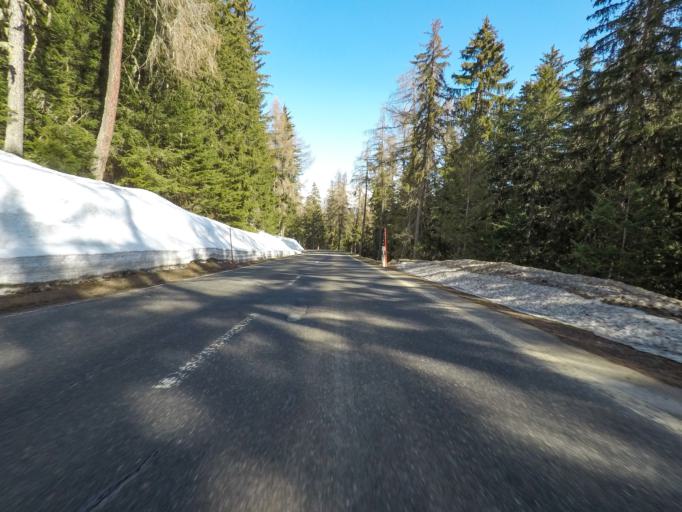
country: CH
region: Valais
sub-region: Herens District
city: Heremence
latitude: 46.1917
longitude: 7.3848
